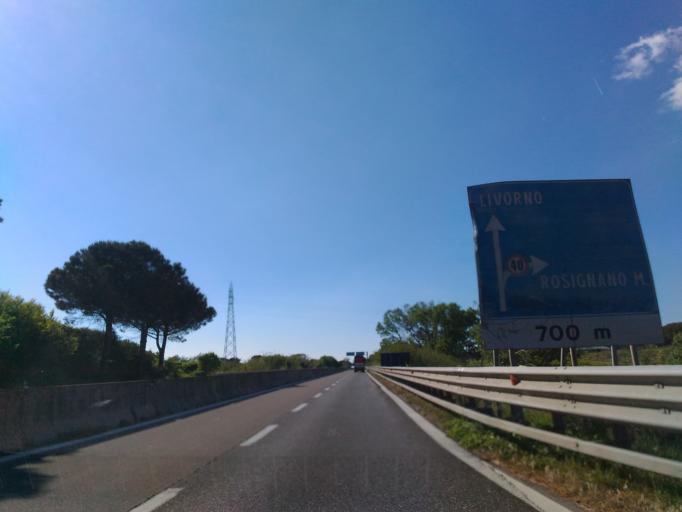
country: IT
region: Tuscany
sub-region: Provincia di Livorno
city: Rosignano Marittimo
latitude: 43.3908
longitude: 10.4767
